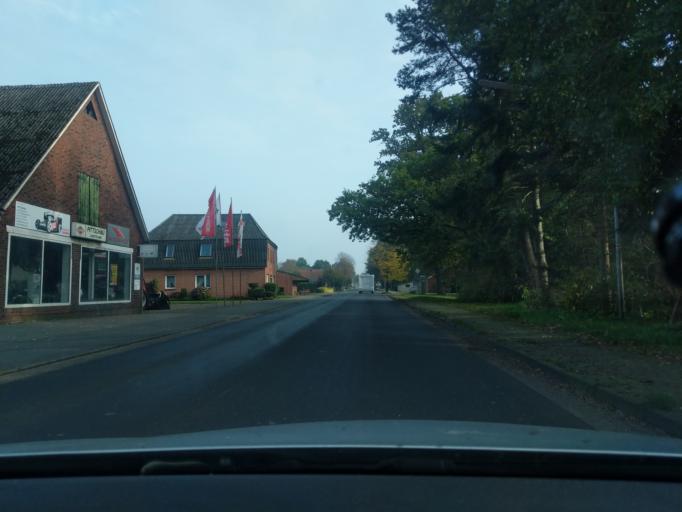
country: DE
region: Lower Saxony
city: Mittelstenahe
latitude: 53.6511
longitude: 9.0390
